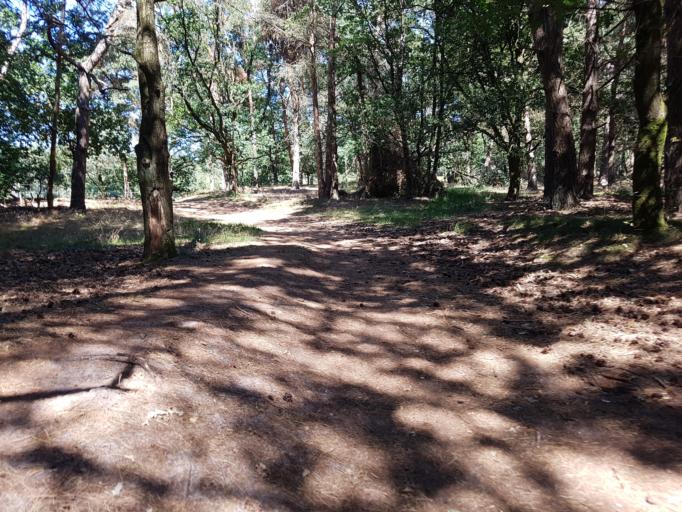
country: NL
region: North Brabant
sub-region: Gemeente Haaren
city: Haaren
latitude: 51.5788
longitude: 5.2493
